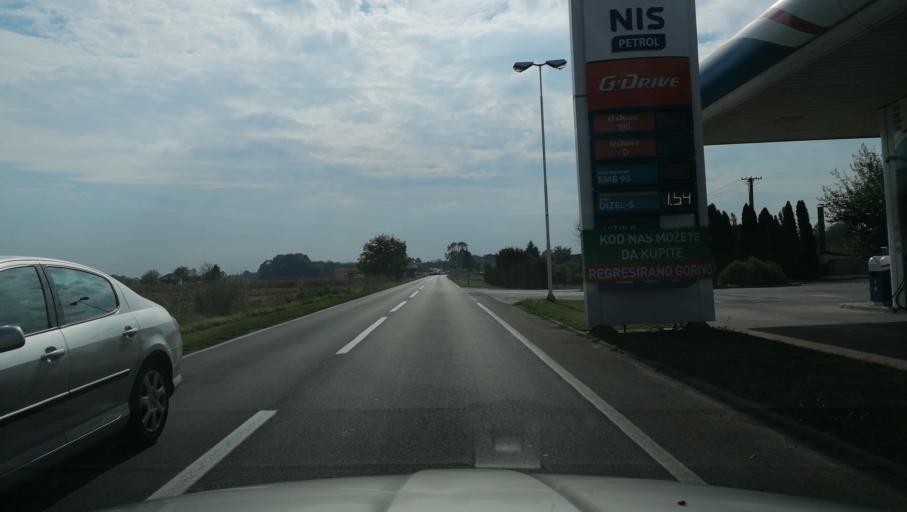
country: BA
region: Republika Srpska
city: Dvorovi
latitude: 44.8368
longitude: 19.2960
